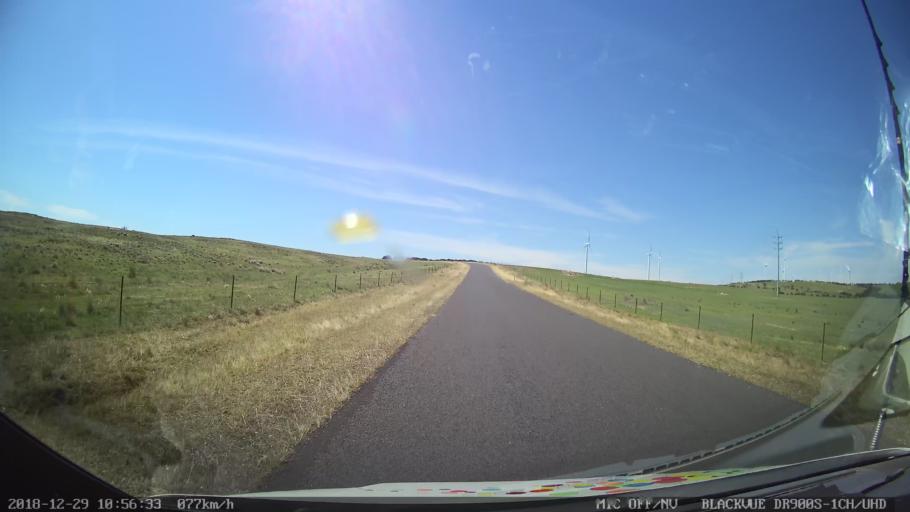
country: AU
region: New South Wales
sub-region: Palerang
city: Bungendore
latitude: -35.1355
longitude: 149.5390
